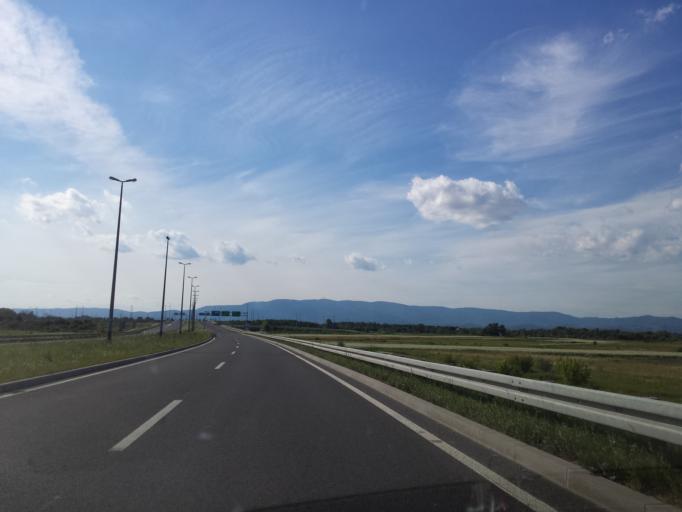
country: HR
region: Zagrebacka
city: Micevec
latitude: 45.7606
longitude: 16.0959
